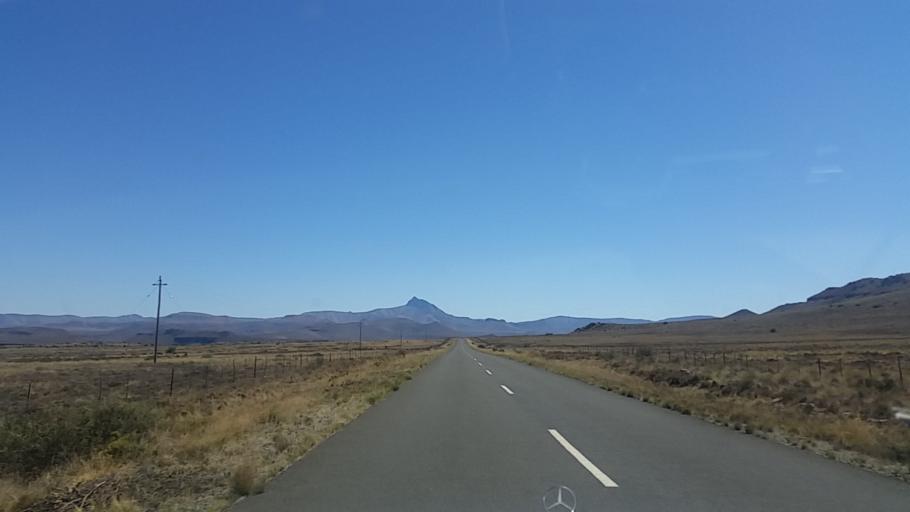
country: ZA
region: Eastern Cape
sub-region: Cacadu District Municipality
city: Graaff-Reinet
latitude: -31.9265
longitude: 24.6022
